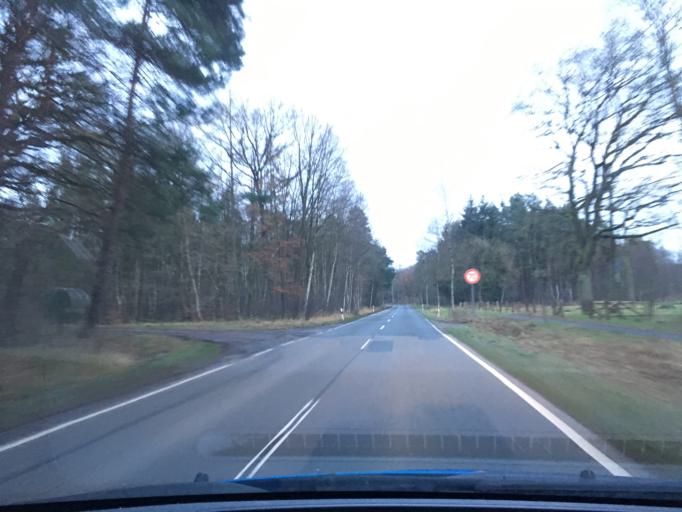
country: DE
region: Lower Saxony
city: Radbruch
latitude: 53.3193
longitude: 10.2418
